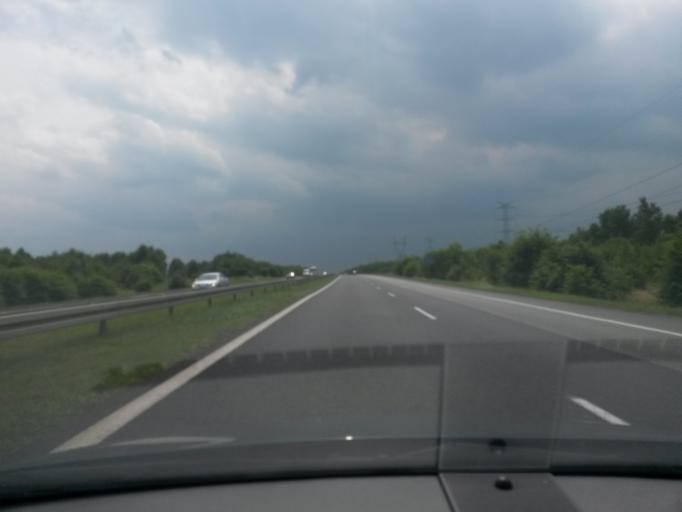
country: PL
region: Lodz Voivodeship
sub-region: Powiat radomszczanski
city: Radomsko
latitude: 51.0956
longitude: 19.3797
